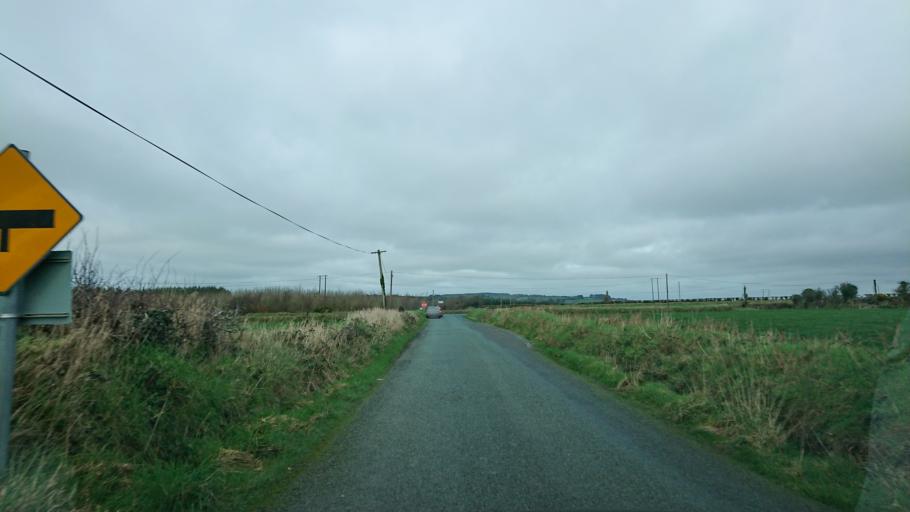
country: IE
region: Munster
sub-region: Waterford
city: Portlaw
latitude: 52.1807
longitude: -7.3028
